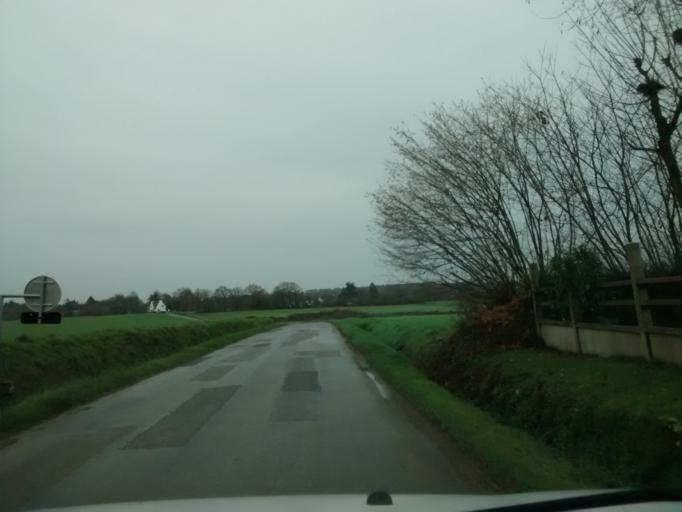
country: FR
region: Brittany
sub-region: Departement d'Ille-et-Vilaine
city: Acigne
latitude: 48.1452
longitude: -1.5473
